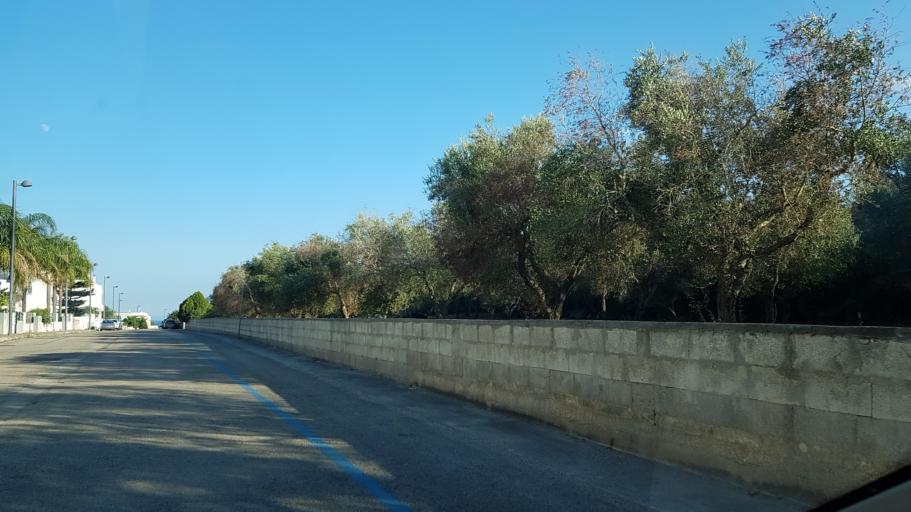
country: IT
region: Apulia
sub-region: Provincia di Lecce
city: Castro
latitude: 40.0060
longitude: 18.4193
